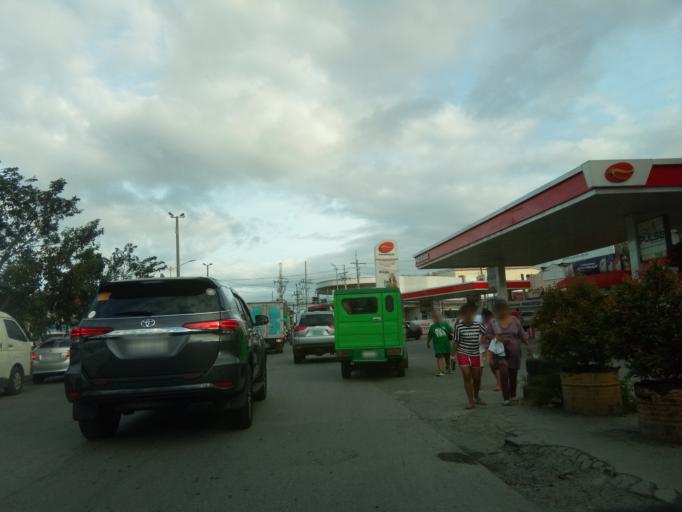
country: PH
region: Calabarzon
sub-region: Province of Cavite
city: Imus
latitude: 14.3861
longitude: 120.9771
